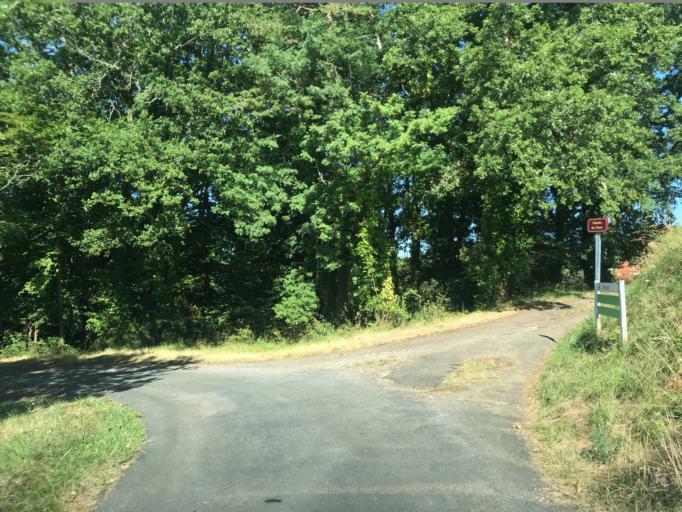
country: FR
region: Aquitaine
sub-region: Departement de la Dordogne
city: Sarlat-la-Caneda
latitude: 44.9078
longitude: 1.1490
